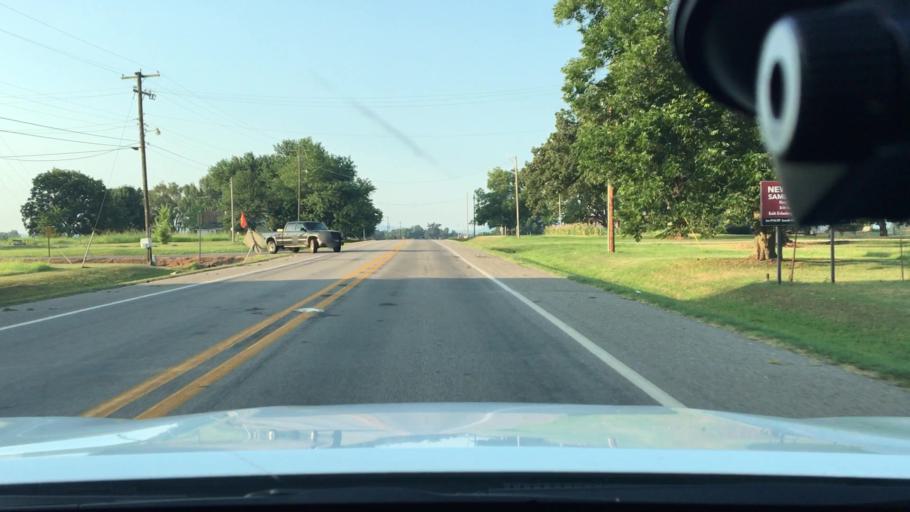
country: US
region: Arkansas
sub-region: Johnson County
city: Clarksville
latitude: 35.3862
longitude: -93.5298
